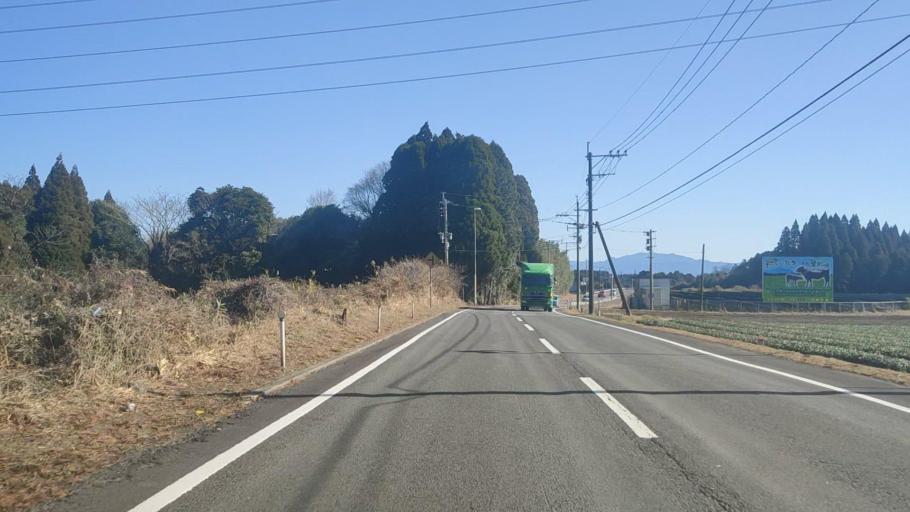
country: JP
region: Kagoshima
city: Sueyoshicho-ninokata
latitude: 31.6886
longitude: 130.9547
